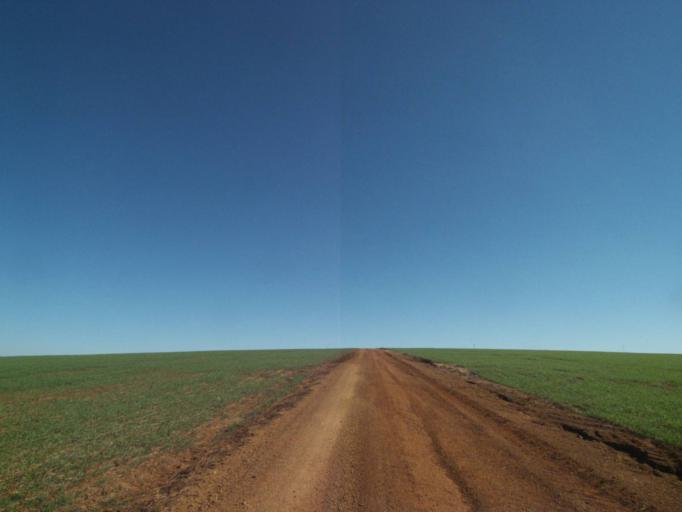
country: BR
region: Parana
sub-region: Tibagi
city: Tibagi
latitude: -24.3881
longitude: -50.3304
